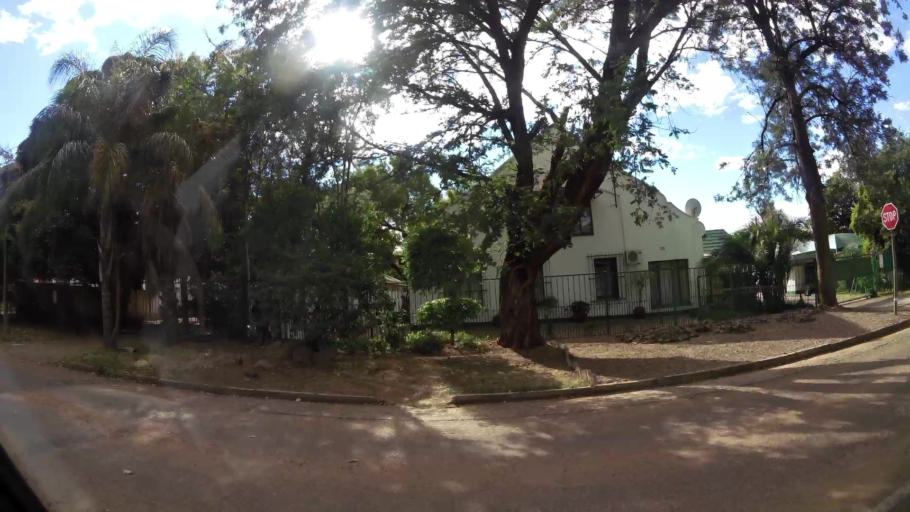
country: ZA
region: Limpopo
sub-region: Waterberg District Municipality
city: Bela-Bela
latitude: -24.8786
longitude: 28.2924
